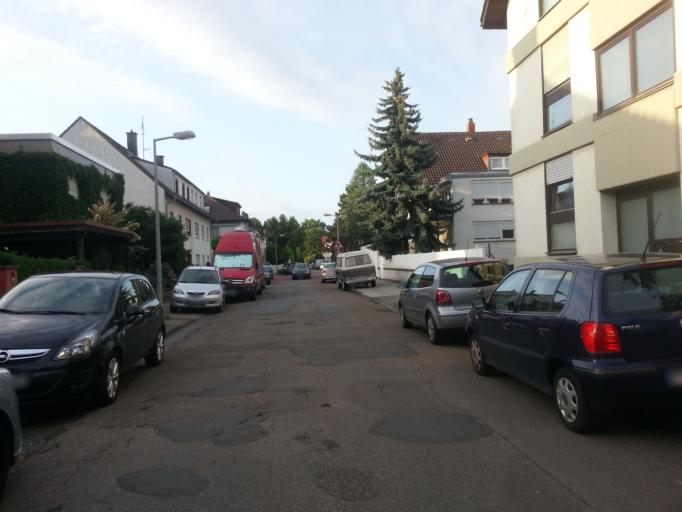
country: DE
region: Baden-Wuerttemberg
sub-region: Karlsruhe Region
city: Mannheim
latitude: 49.4802
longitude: 8.5070
